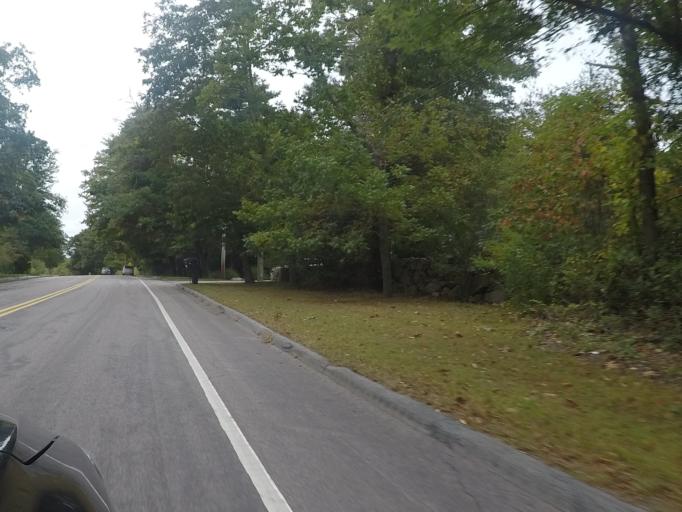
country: US
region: Massachusetts
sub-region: Bristol County
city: Smith Mills
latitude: 41.6346
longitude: -71.0017
